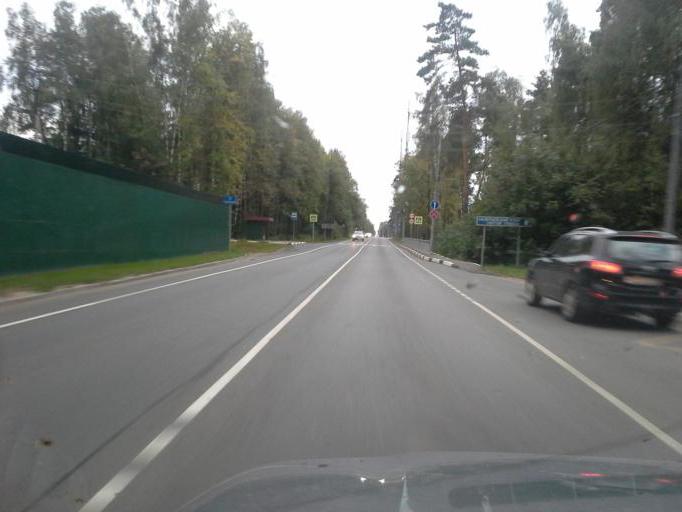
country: RU
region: Moskovskaya
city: Nazar'yevo
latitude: 55.6984
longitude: 37.0649
